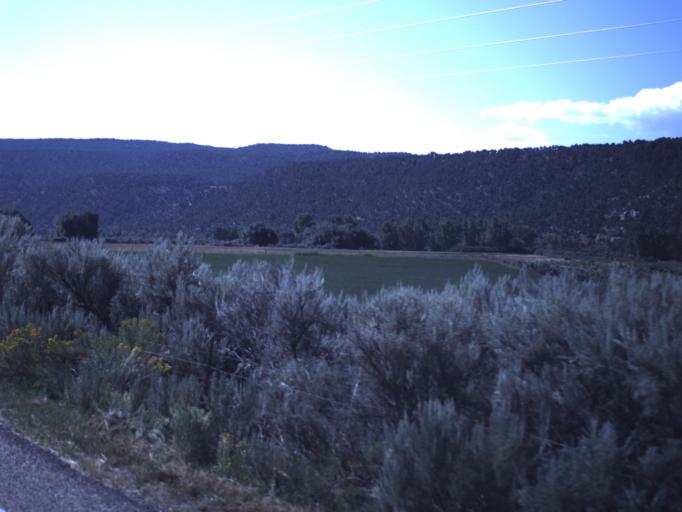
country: US
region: Utah
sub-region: Duchesne County
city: Duchesne
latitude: 40.3252
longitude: -110.6622
